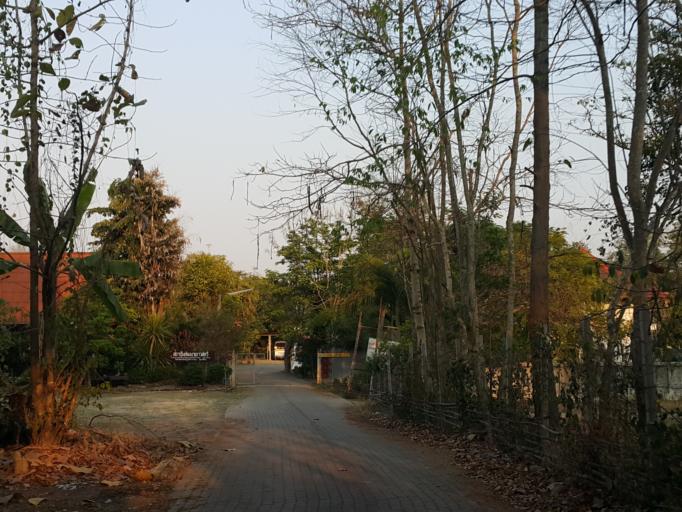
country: TH
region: Chiang Mai
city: San Sai
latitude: 18.9009
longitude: 98.9554
